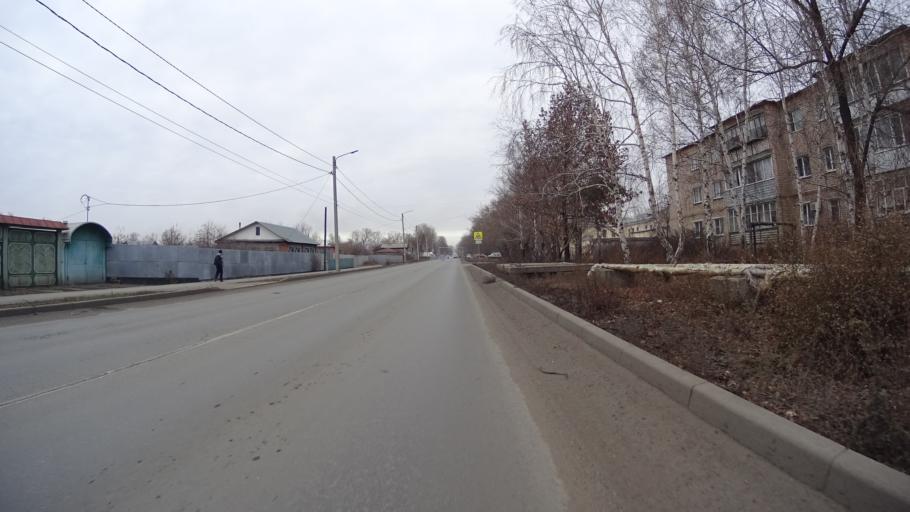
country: RU
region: Chelyabinsk
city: Troitsk
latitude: 54.1093
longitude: 61.5709
